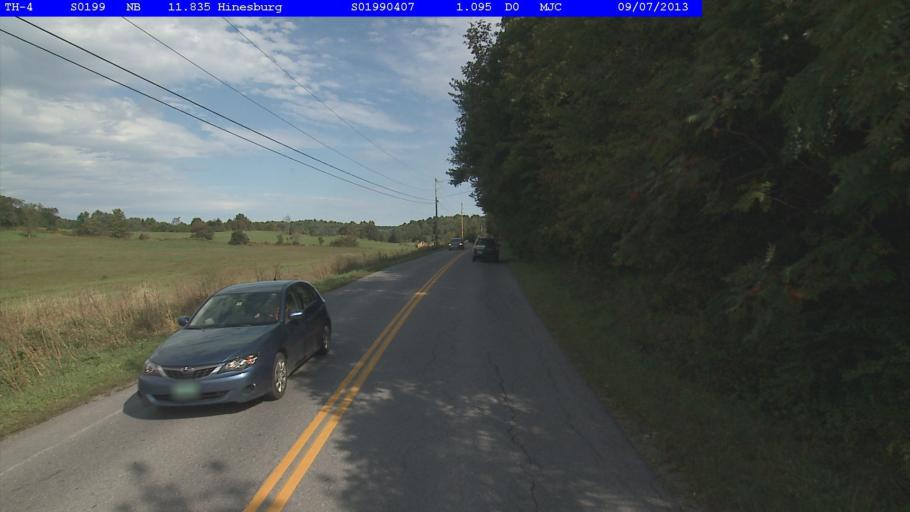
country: US
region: Vermont
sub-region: Chittenden County
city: Hinesburg
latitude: 44.2937
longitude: -73.1084
